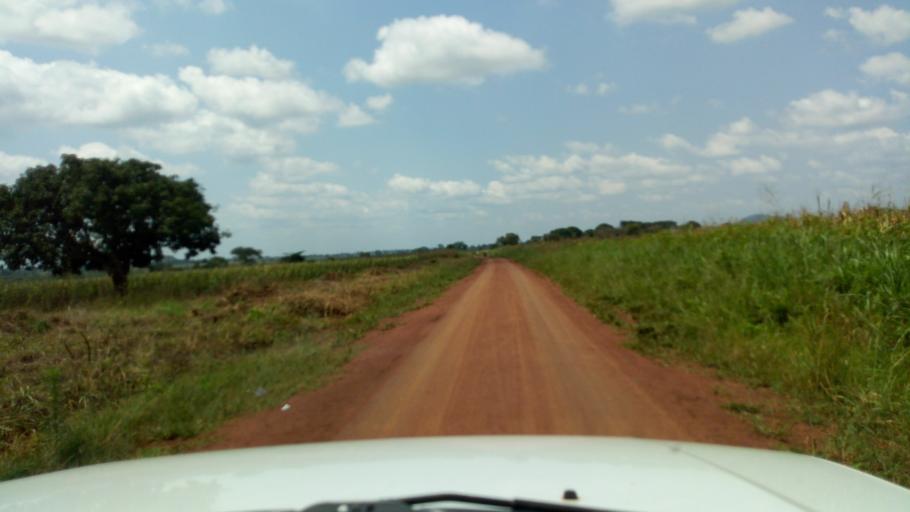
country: UG
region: Western Region
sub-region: Masindi District
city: Masindi
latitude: 1.7541
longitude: 31.8578
